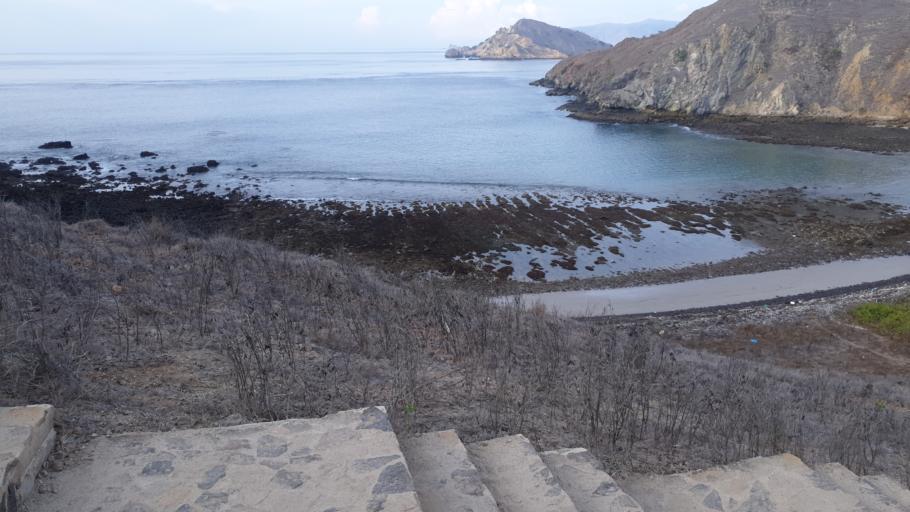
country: ID
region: East Nusa Tenggara
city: Komodo
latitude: -8.6778
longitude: 119.5554
